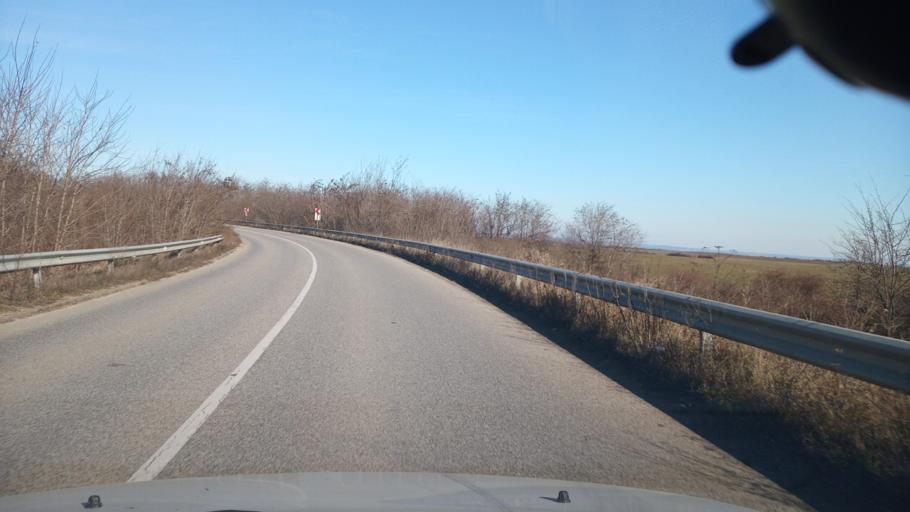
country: BG
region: Pleven
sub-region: Obshtina Pleven
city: Pleven
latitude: 43.4290
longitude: 24.7193
